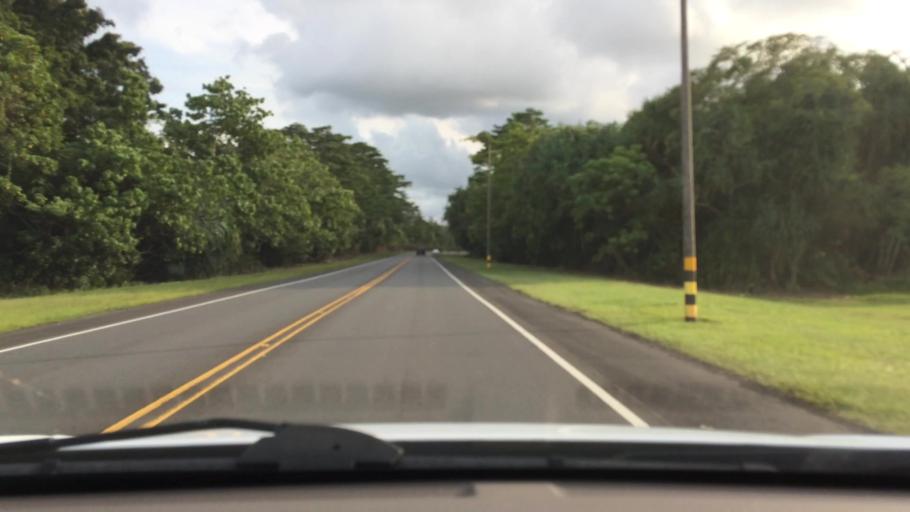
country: US
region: Hawaii
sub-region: Hawaii County
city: Hilo
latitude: 19.7136
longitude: -155.0564
